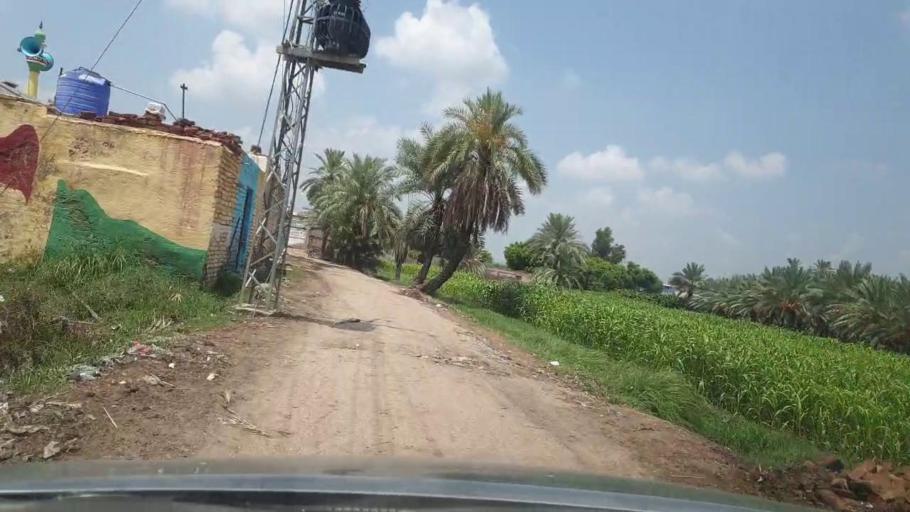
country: PK
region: Sindh
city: Pir jo Goth
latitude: 27.6079
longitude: 68.6133
